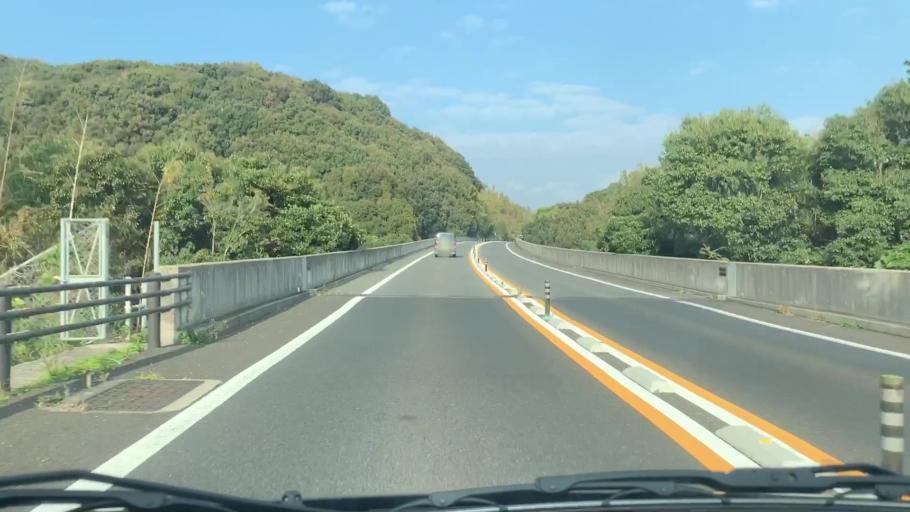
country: JP
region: Nagasaki
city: Sasebo
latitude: 33.0300
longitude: 129.7388
